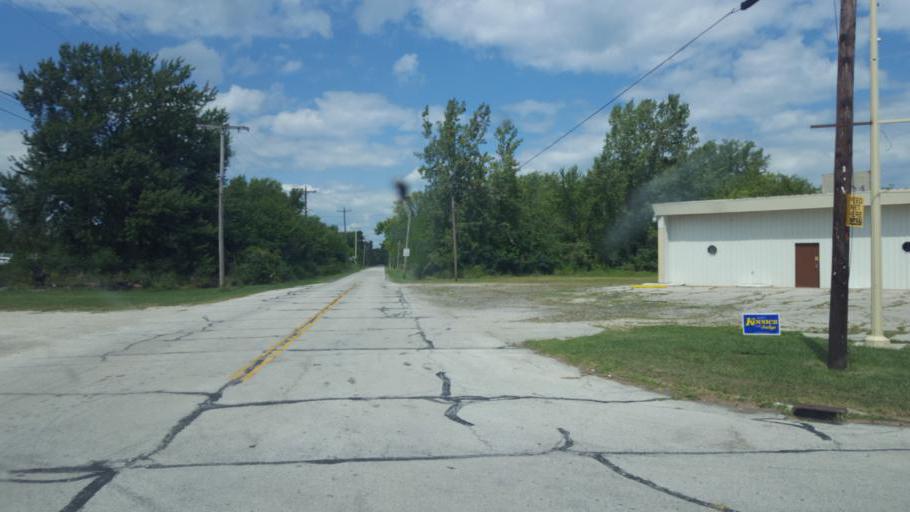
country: US
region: Ohio
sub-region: Lucas County
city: Curtice
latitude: 41.6611
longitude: -83.2738
